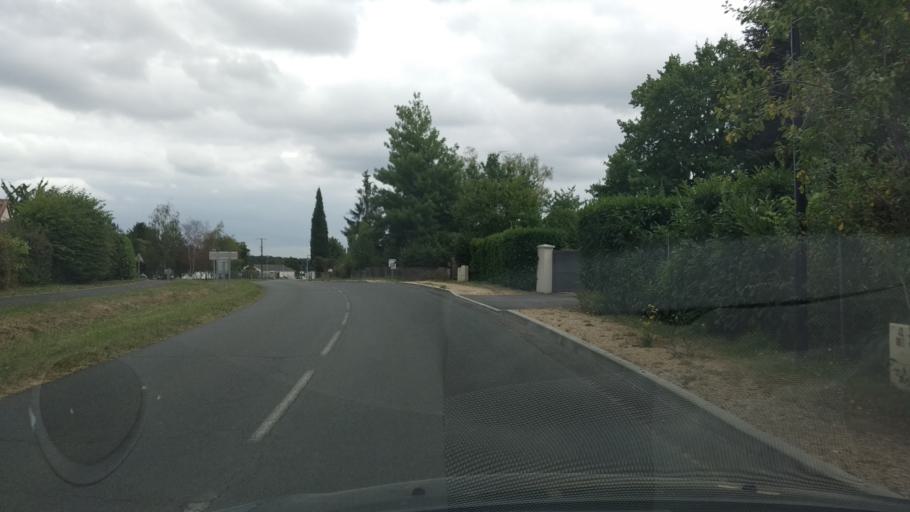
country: FR
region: Poitou-Charentes
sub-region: Departement de la Vienne
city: Smarves
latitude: 46.5078
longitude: 0.3576
